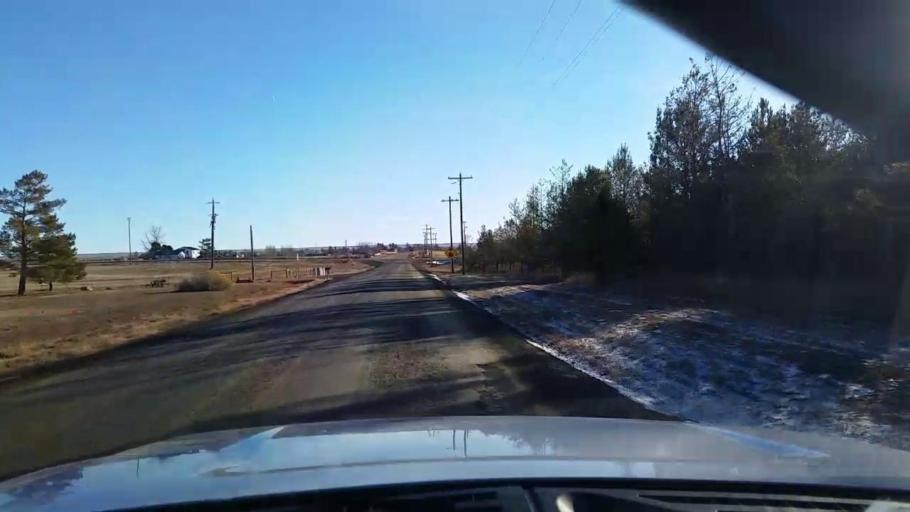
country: US
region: Colorado
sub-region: Larimer County
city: Wellington
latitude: 40.7696
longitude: -105.0788
